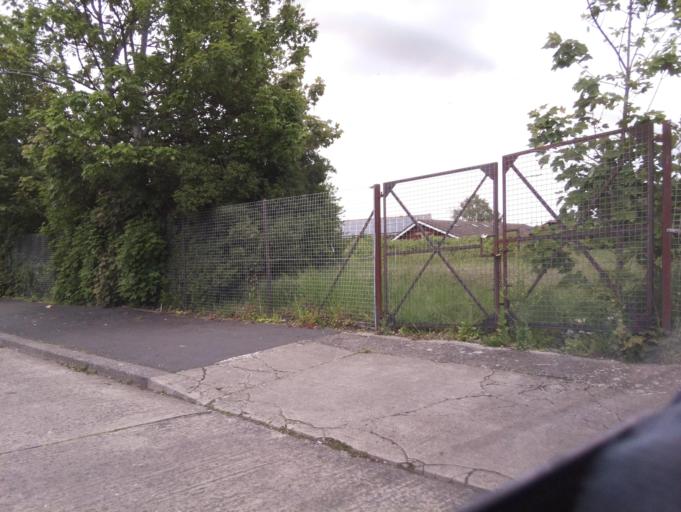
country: GB
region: England
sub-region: Bristol
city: Bristol
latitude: 51.5047
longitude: -2.6023
